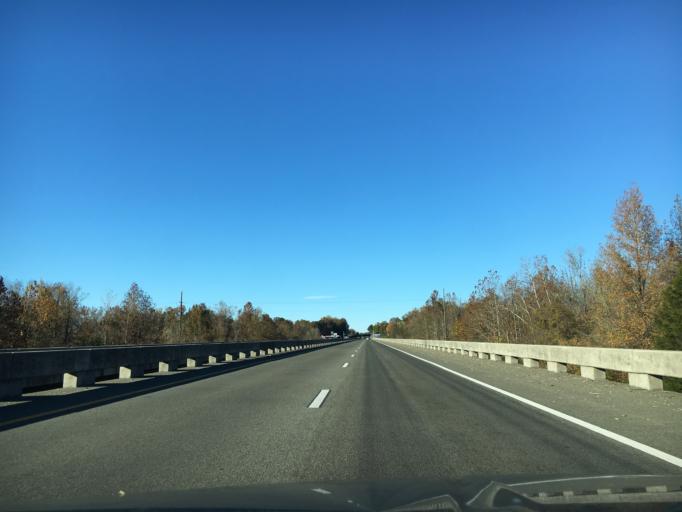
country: US
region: Virginia
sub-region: Halifax County
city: South Boston
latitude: 36.6919
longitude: -78.8874
